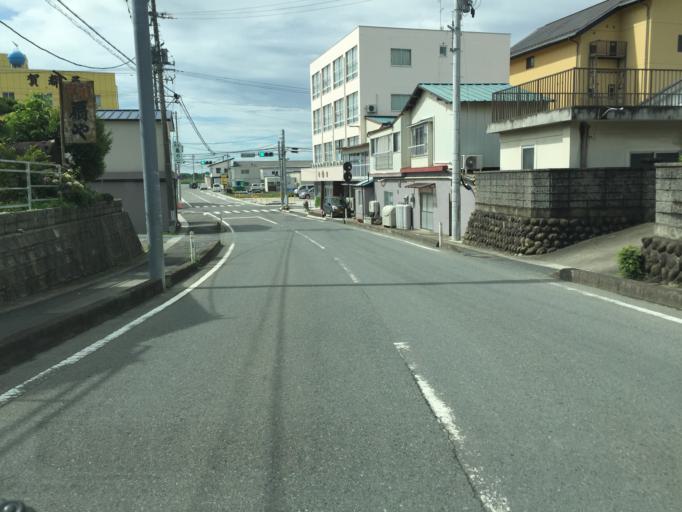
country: JP
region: Miyagi
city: Marumori
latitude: 37.8235
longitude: 140.9682
